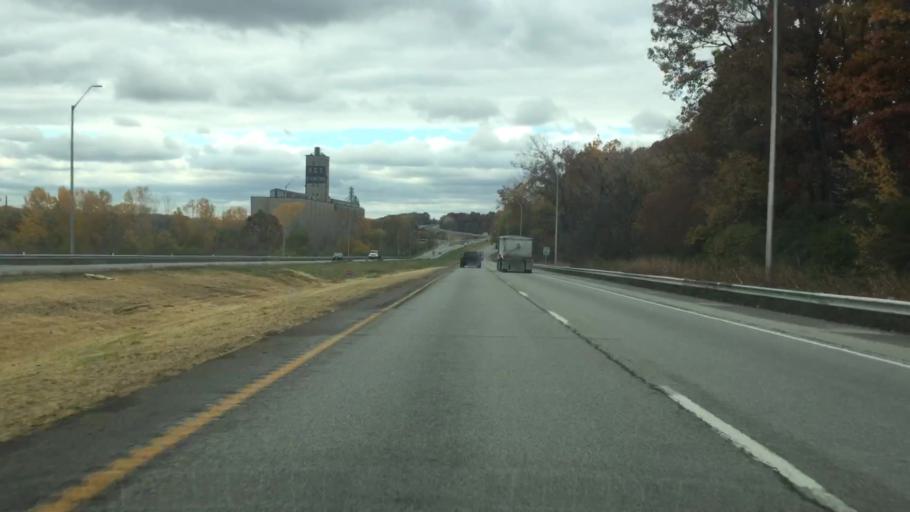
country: US
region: Missouri
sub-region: Clay County
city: Claycomo
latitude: 39.1555
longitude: -94.5056
